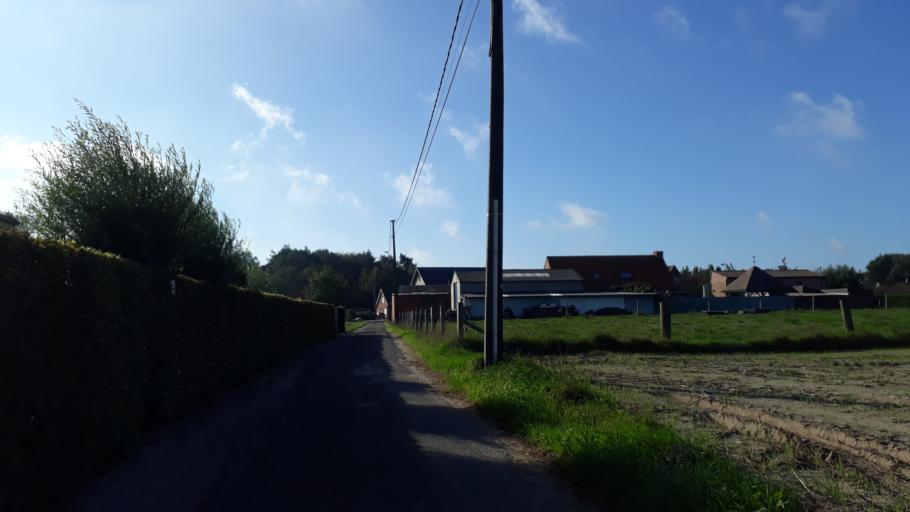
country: BE
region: Flanders
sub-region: Provincie West-Vlaanderen
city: Lichtervelde
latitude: 51.0637
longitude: 3.1383
